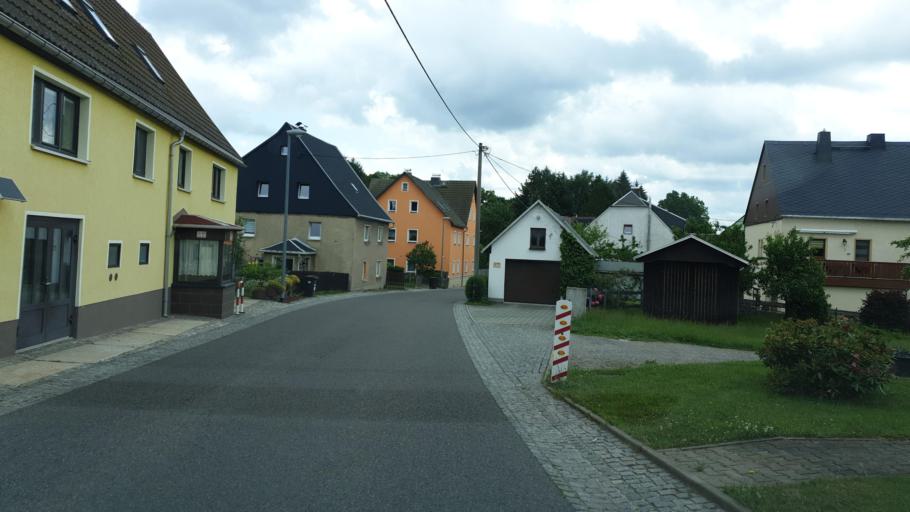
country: DE
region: Saxony
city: Marienberg
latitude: 50.6819
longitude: 13.1657
